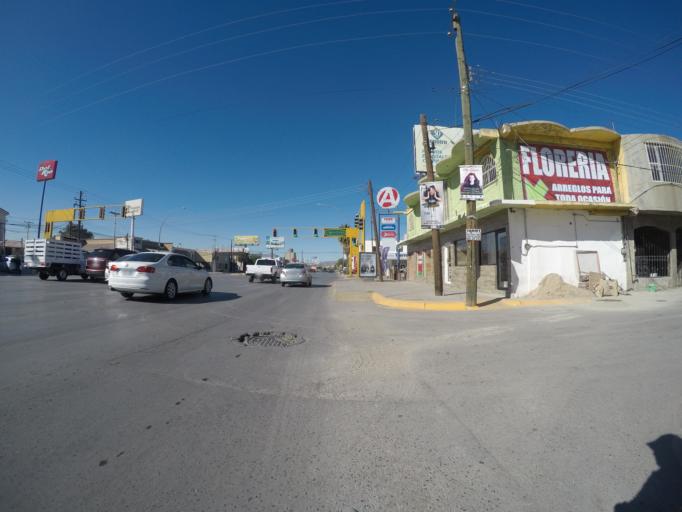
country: MX
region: Chihuahua
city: Ciudad Juarez
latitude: 31.7382
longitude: -106.4376
